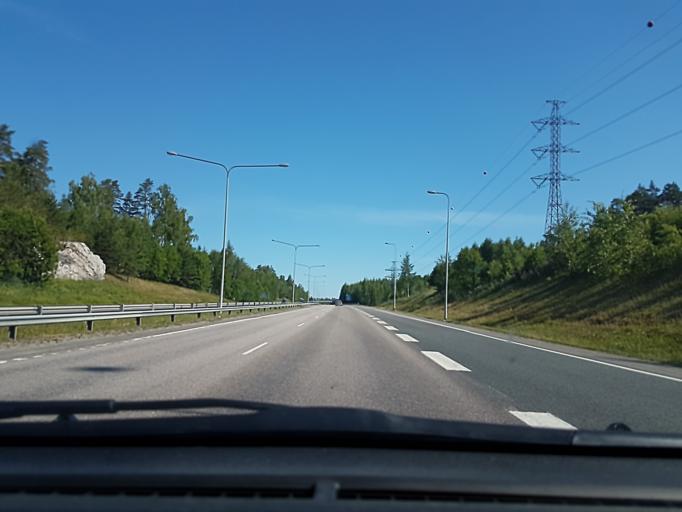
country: FI
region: Uusimaa
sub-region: Helsinki
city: Vantaa
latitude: 60.3267
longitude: 24.9985
